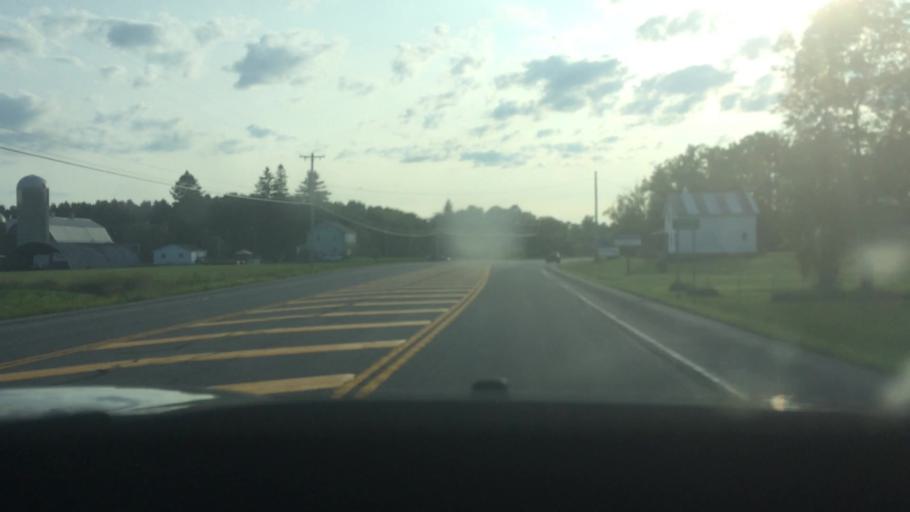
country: US
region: New York
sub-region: St. Lawrence County
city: Ogdensburg
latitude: 44.6725
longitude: -75.4214
